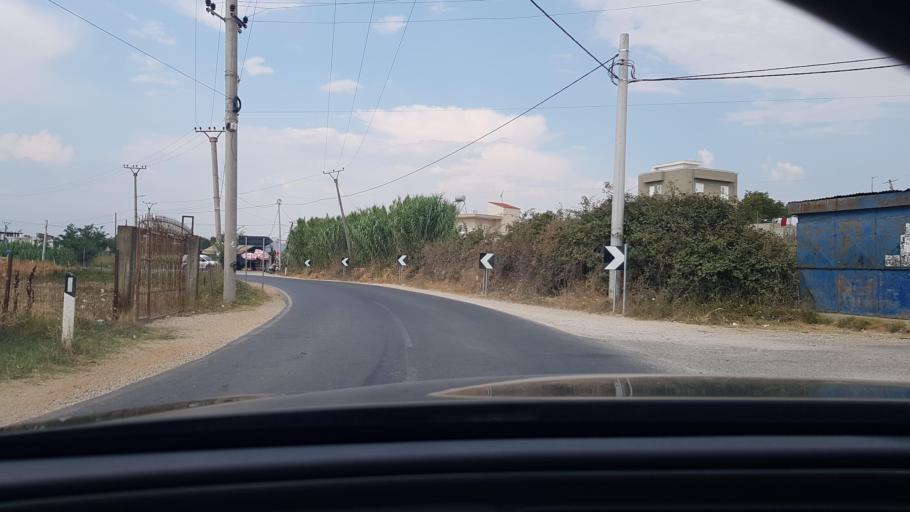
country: AL
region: Durres
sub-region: Rrethi i Durresit
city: Katundi i Ri
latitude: 41.4205
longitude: 19.5486
